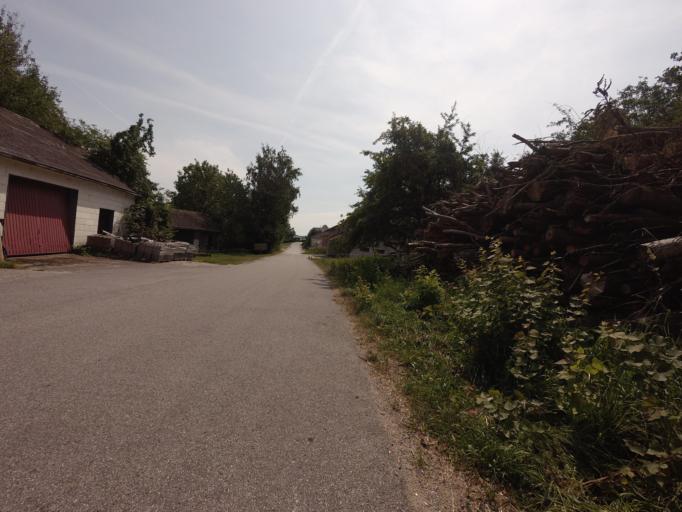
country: AT
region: Upper Austria
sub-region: Politischer Bezirk Urfahr-Umgebung
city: Schenkenfelden
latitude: 48.5239
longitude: 14.3604
